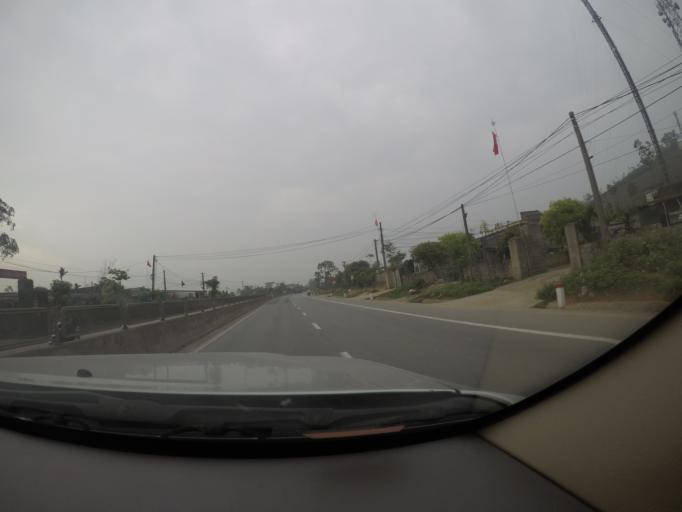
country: VN
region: Ha Tinh
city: Ky Anh
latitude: 18.1610
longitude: 106.2391
